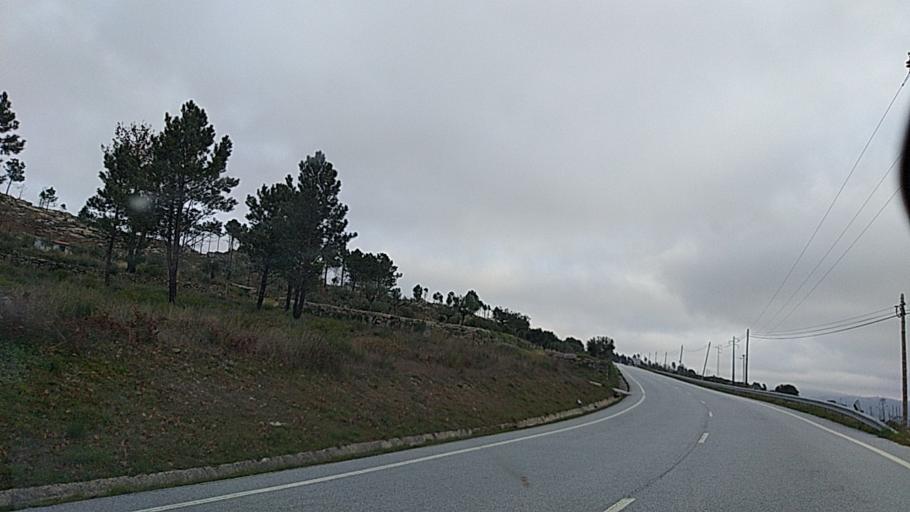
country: PT
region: Guarda
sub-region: Fornos de Algodres
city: Fornos de Algodres
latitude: 40.6600
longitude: -7.4792
